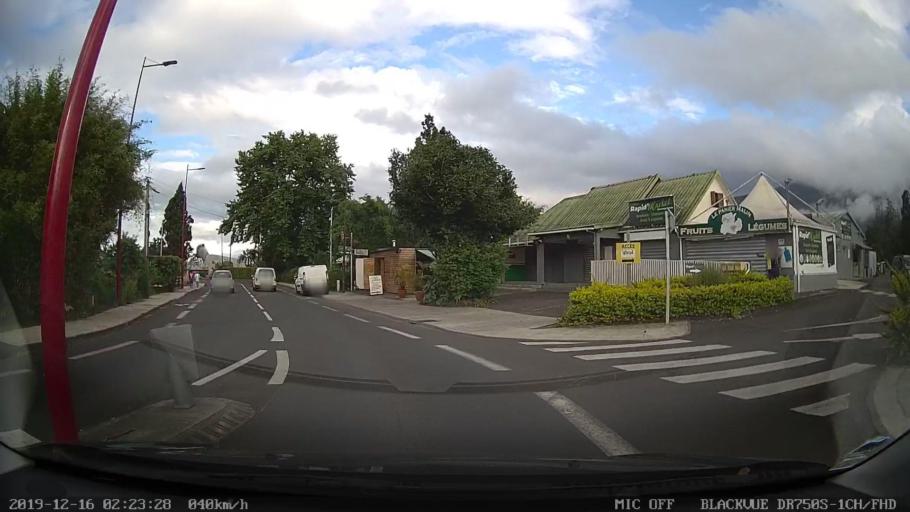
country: RE
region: Reunion
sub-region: Reunion
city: Salazie
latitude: -21.1428
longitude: 55.6211
